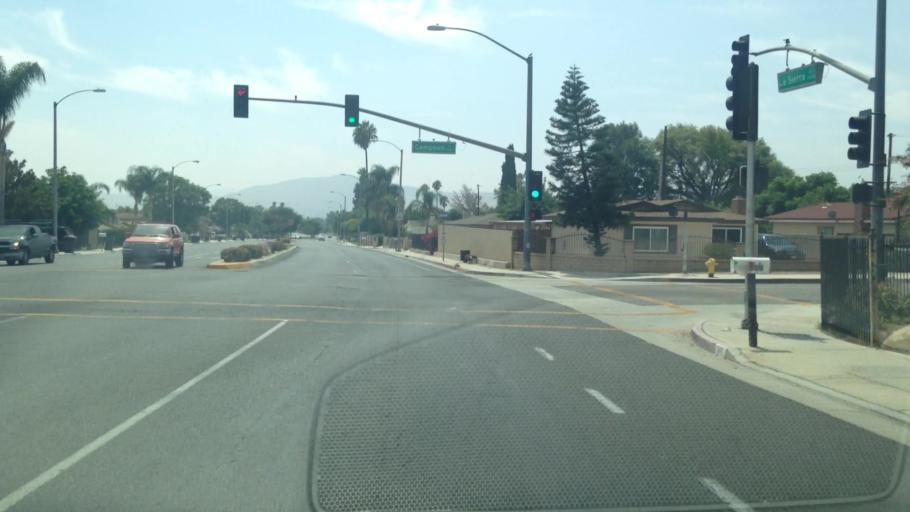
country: US
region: California
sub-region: Riverside County
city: Pedley
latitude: 33.9326
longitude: -117.4957
